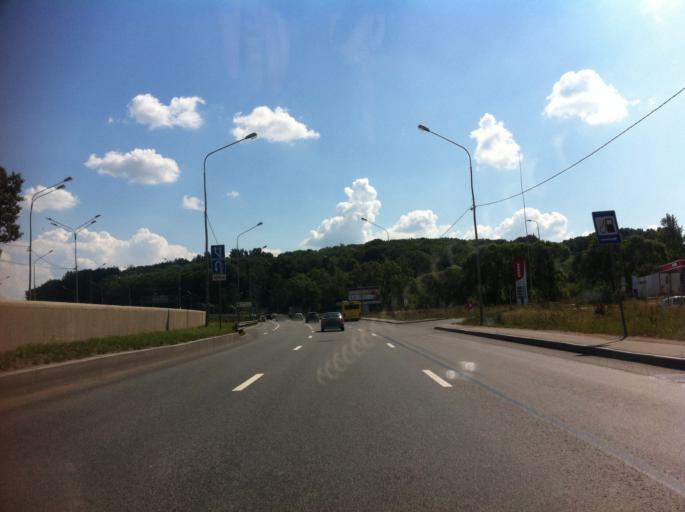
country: RU
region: St.-Petersburg
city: Aleksandrovskaya
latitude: 59.7786
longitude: 30.3250
